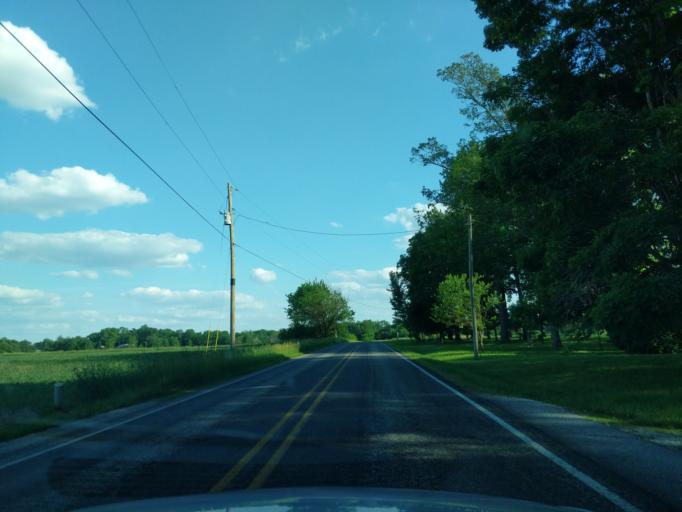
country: US
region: Indiana
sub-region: Kosciusko County
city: North Webster
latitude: 41.3033
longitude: -85.6433
